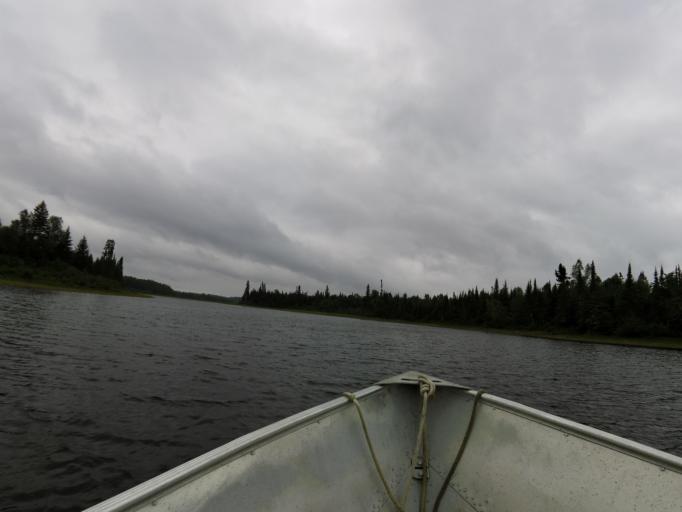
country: CA
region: Ontario
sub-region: Rainy River District
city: Atikokan
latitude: 49.5960
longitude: -91.3404
